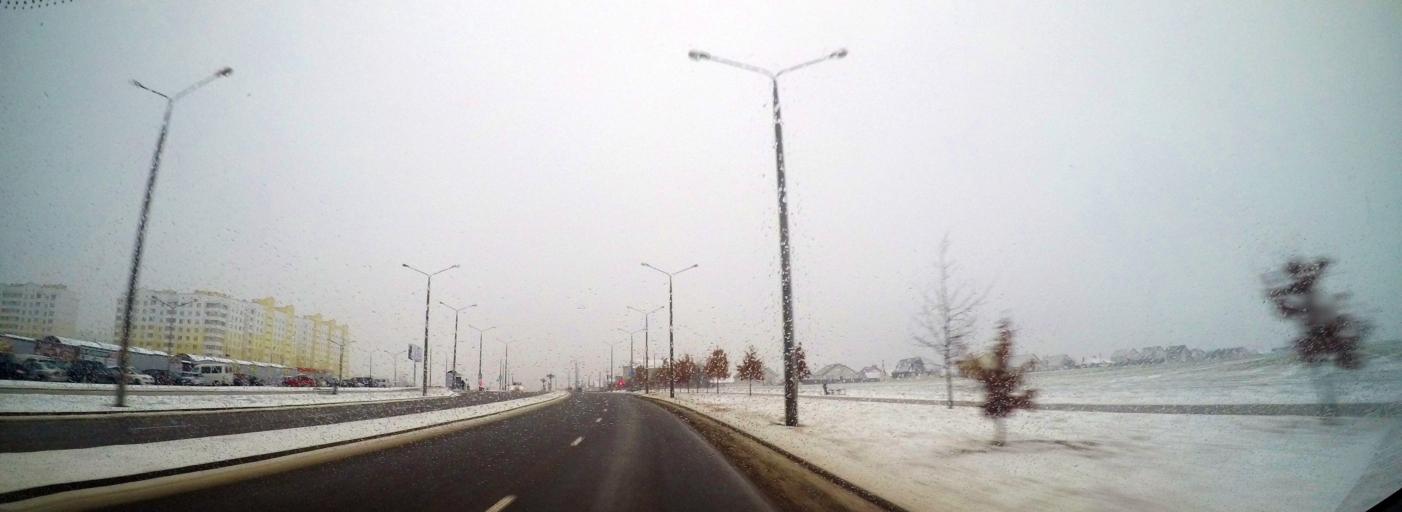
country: BY
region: Grodnenskaya
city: Hrodna
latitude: 53.6240
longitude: 23.8150
